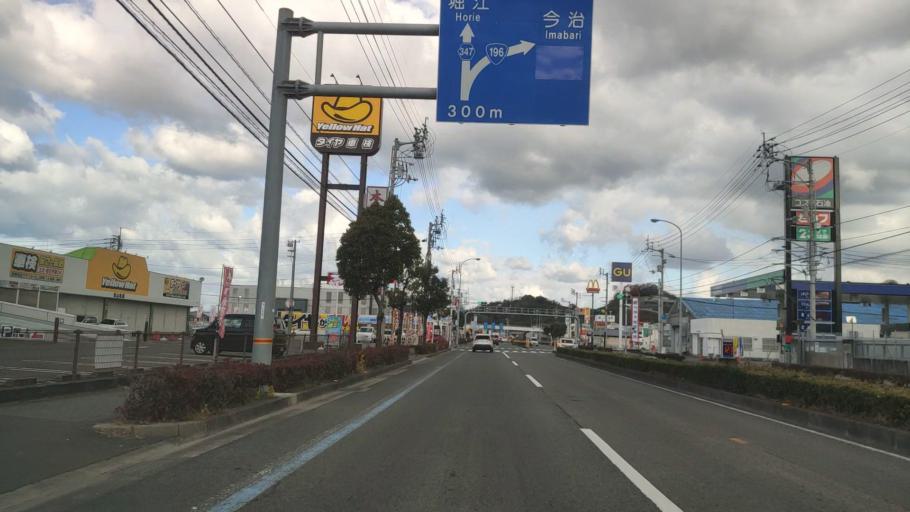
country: JP
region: Ehime
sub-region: Shikoku-chuo Shi
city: Matsuyama
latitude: 33.8832
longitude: 132.7518
